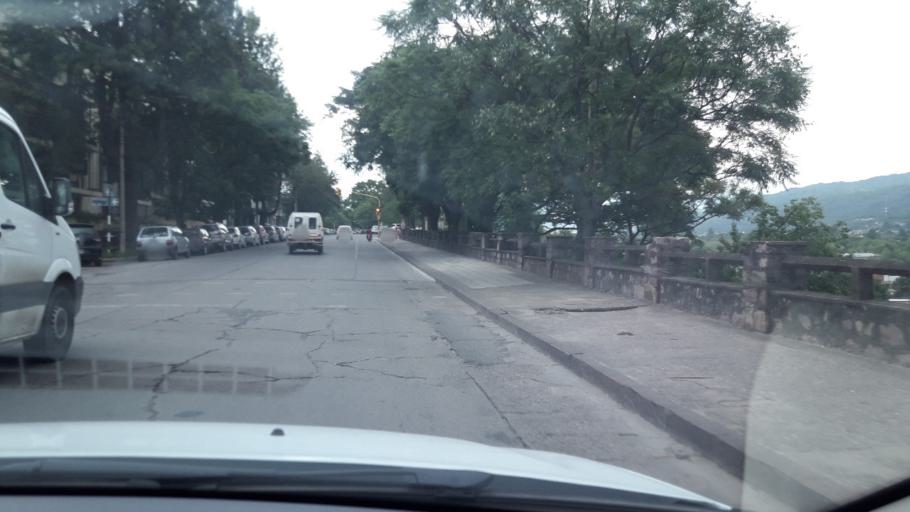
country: AR
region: Jujuy
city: San Salvador de Jujuy
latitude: -24.1799
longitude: -65.3135
